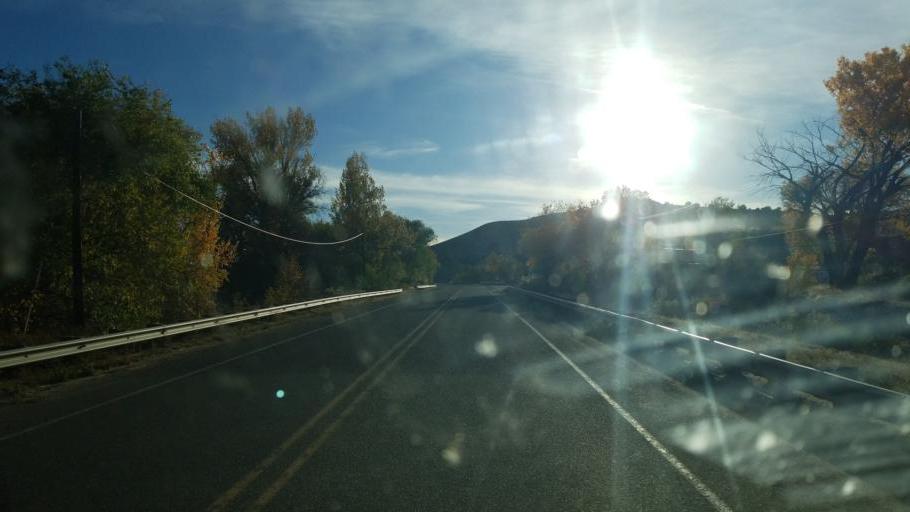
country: US
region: New Mexico
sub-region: San Juan County
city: Bloomfield
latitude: 36.7223
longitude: -107.8307
